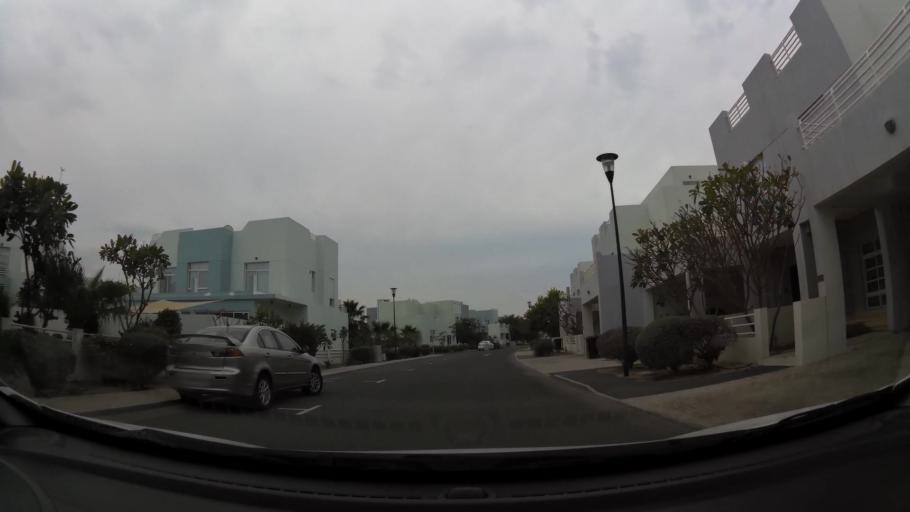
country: BH
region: Northern
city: Ar Rifa'
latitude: 26.1008
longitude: 50.5617
